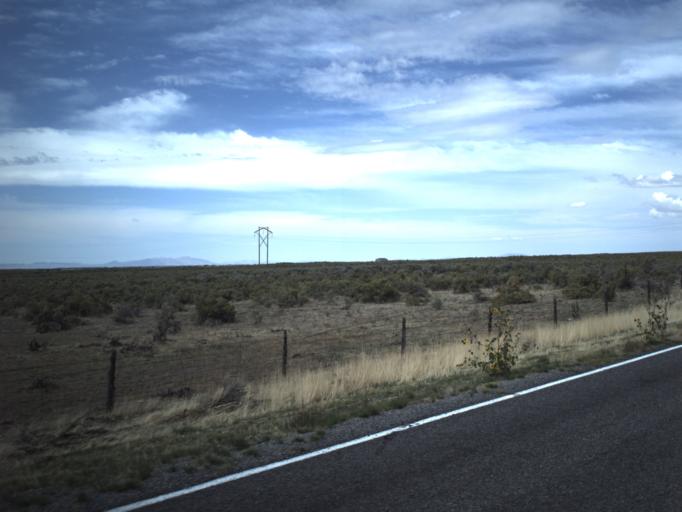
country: US
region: Utah
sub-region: Millard County
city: Fillmore
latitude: 39.1516
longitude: -112.4099
